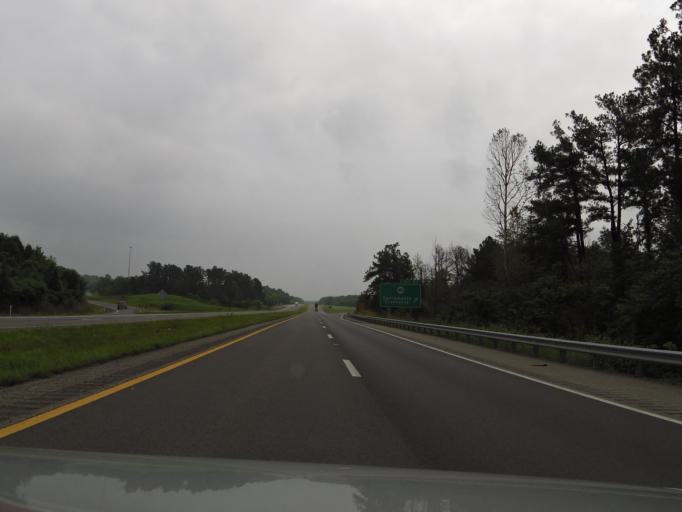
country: US
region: Kentucky
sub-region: Muhlenberg County
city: Morehead
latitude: 37.2523
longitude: -87.2059
